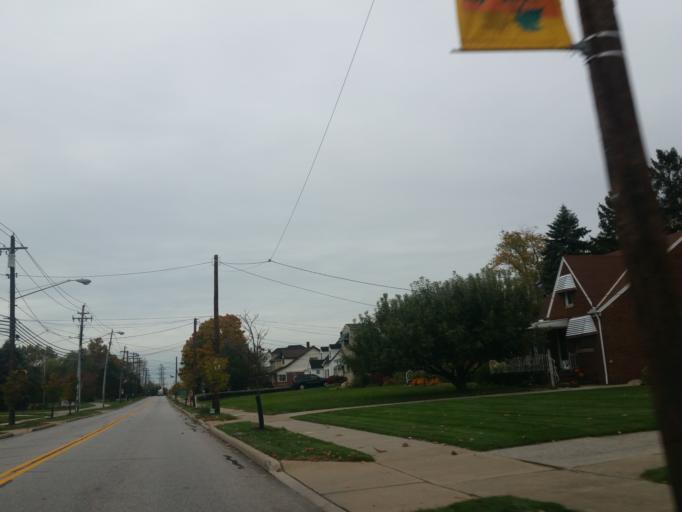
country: US
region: Ohio
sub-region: Cuyahoga County
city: Newburgh Heights
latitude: 41.4345
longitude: -81.6566
